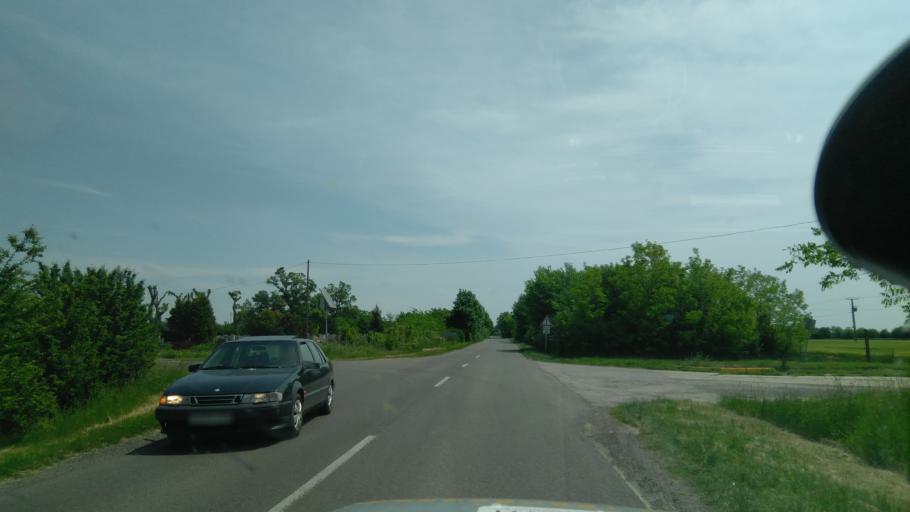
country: HU
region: Csongrad
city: Szekkutas
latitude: 46.5754
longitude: 20.4645
